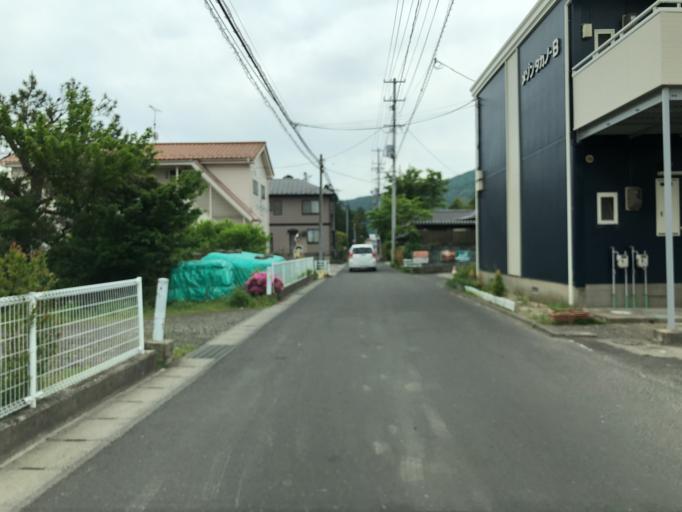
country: JP
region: Fukushima
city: Fukushima-shi
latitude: 37.7883
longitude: 140.4797
